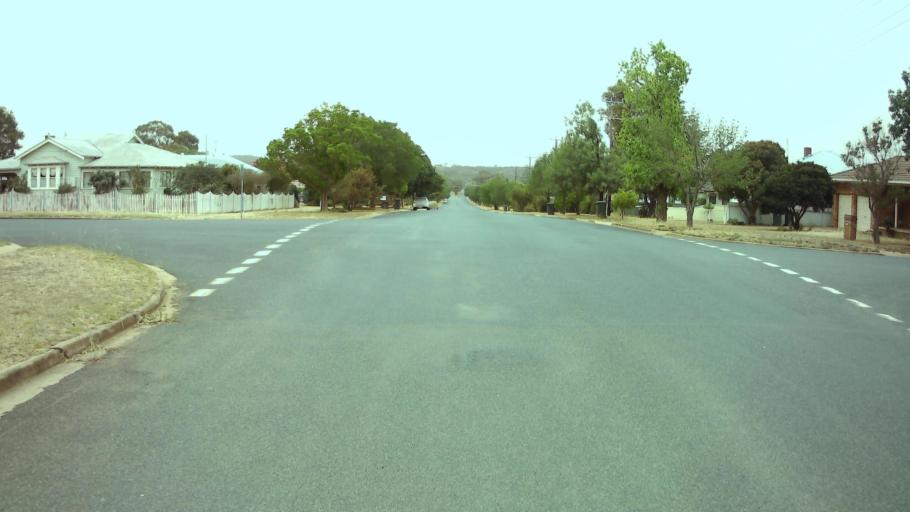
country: AU
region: New South Wales
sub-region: Weddin
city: Grenfell
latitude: -33.9007
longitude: 148.1646
